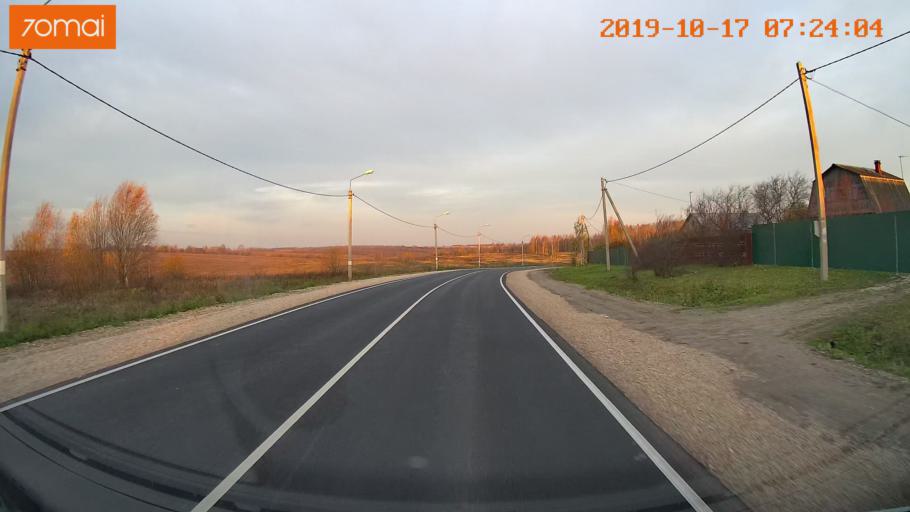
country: RU
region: Vladimir
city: Stavrovo
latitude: 56.3342
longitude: 40.1142
